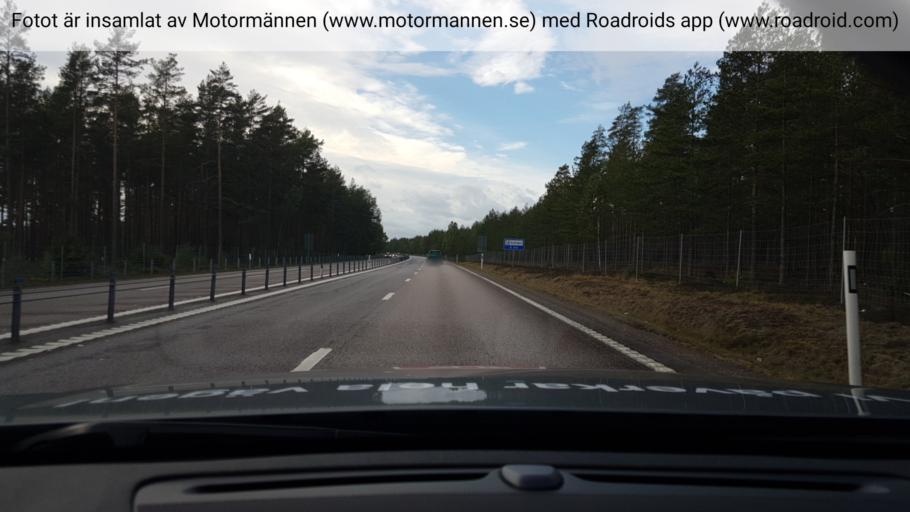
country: SE
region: Vaermland
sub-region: Karlstads Kommun
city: Valberg
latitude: 59.3859
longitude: 13.2249
